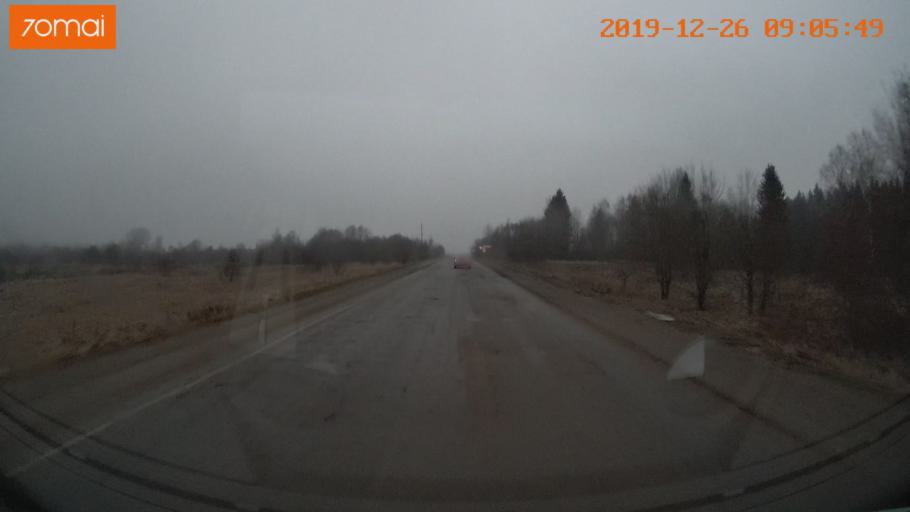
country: RU
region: Vologda
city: Gryazovets
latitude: 58.8296
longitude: 40.2558
